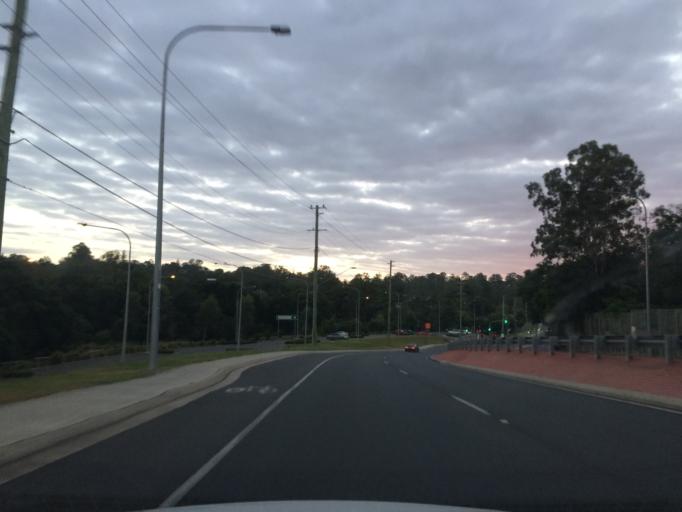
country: AU
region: Queensland
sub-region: Brisbane
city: Kenmore Hills
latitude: -27.5151
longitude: 152.9280
